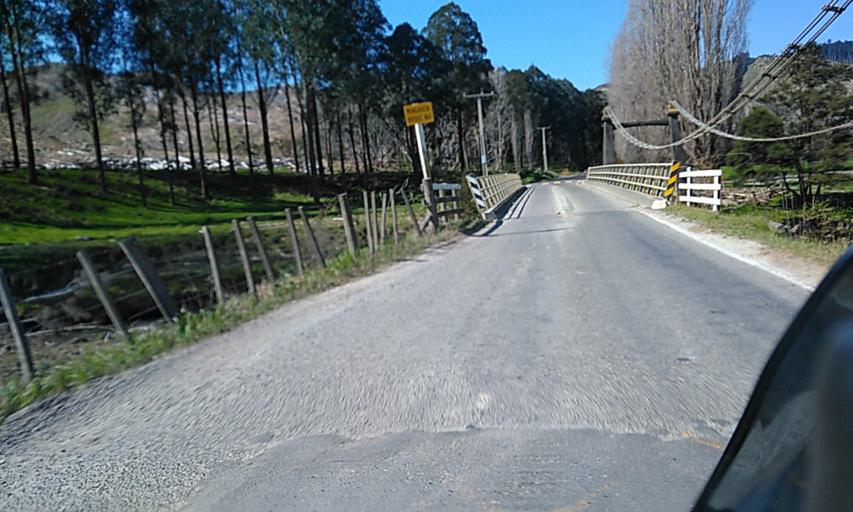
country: NZ
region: Gisborne
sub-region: Gisborne District
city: Gisborne
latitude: -38.3253
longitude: 178.1805
